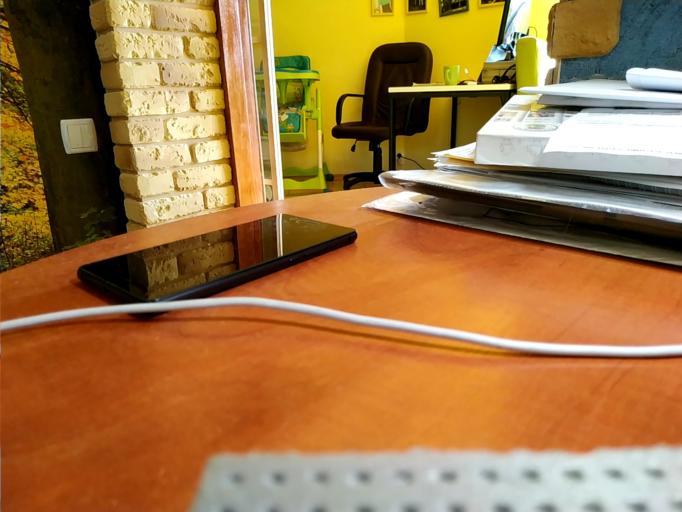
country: RU
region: Tverskaya
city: Likhoslavl'
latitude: 57.3647
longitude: 35.4499
